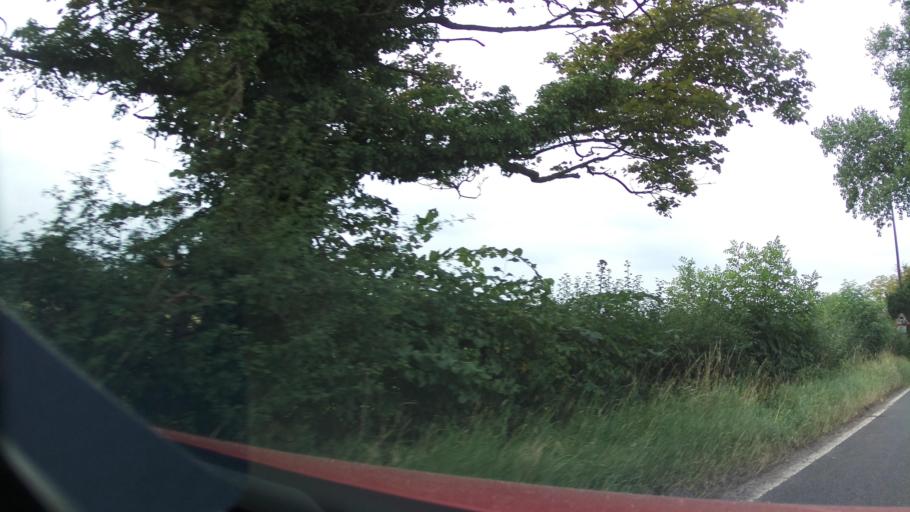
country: GB
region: England
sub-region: Staffordshire
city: Mayfield
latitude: 53.0098
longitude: -1.7526
